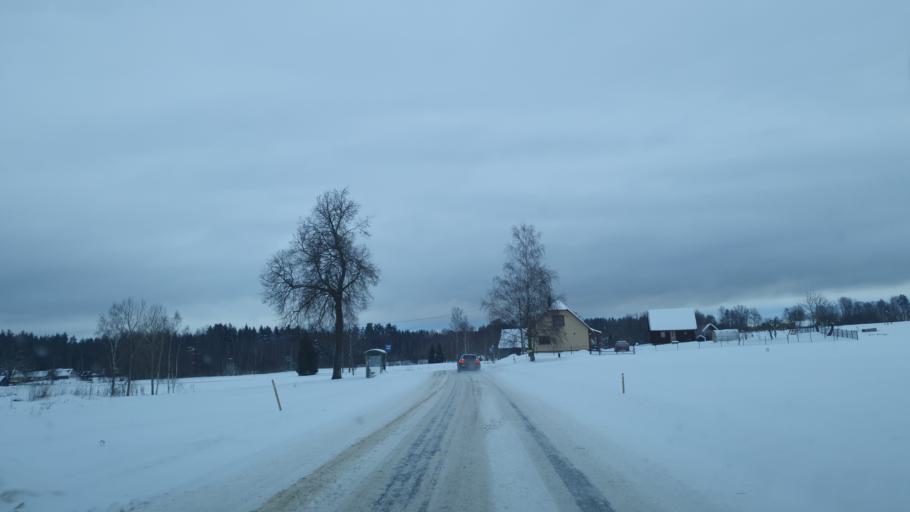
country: EE
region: Polvamaa
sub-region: Polva linn
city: Polva
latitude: 58.1028
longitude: 27.0913
